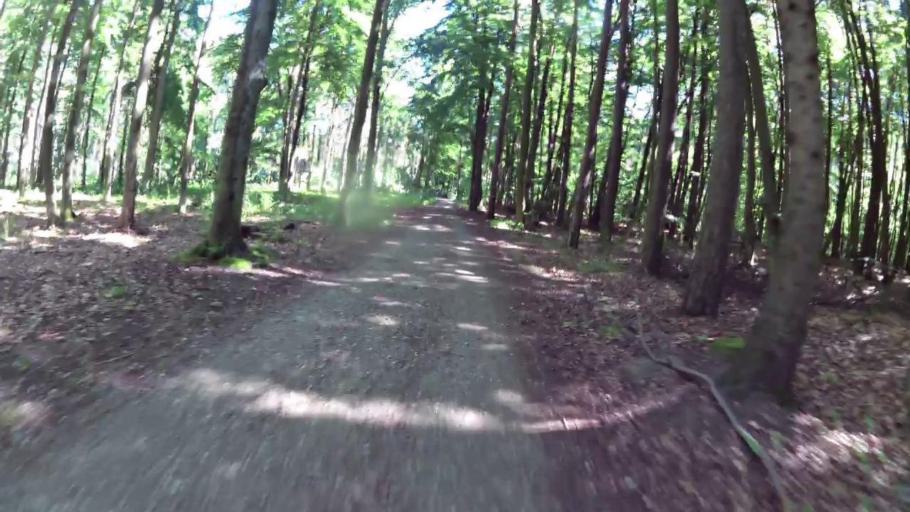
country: PL
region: West Pomeranian Voivodeship
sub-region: Powiat kamienski
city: Dziwnow
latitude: 54.0400
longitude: 14.8270
